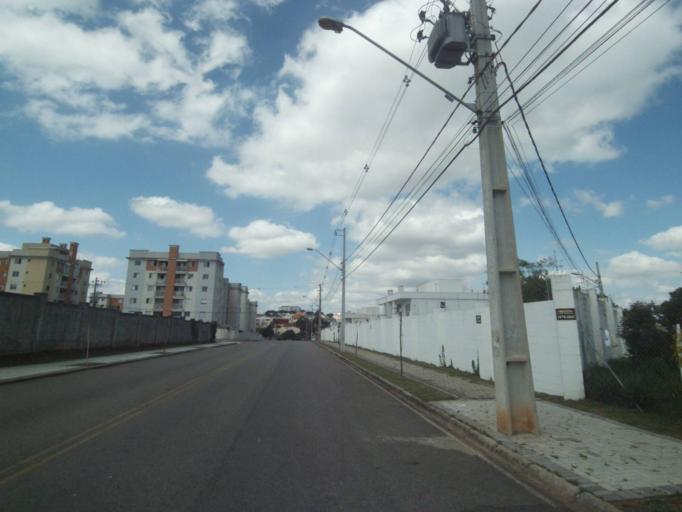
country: BR
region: Parana
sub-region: Curitiba
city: Curitiba
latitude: -25.5052
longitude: -49.3093
